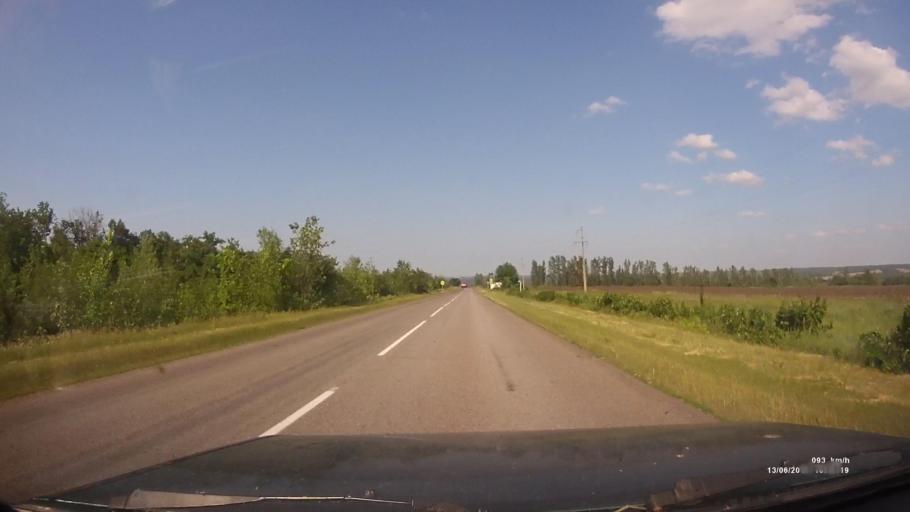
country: RU
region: Rostov
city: Kazanskaya
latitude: 49.9417
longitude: 41.4014
